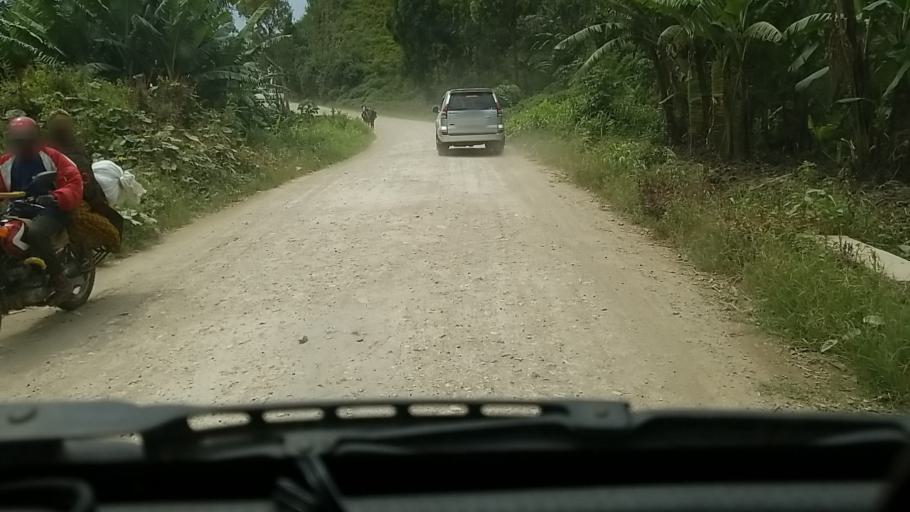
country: CD
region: Nord Kivu
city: Sake
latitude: -1.5922
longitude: 29.0400
